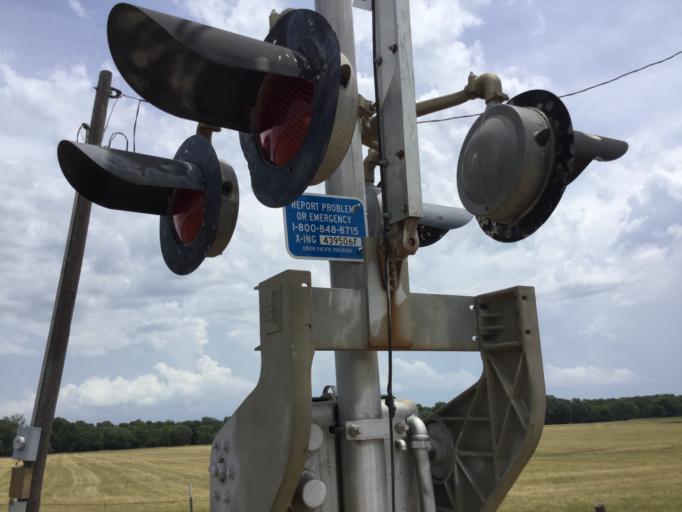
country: US
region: Kansas
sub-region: Woodson County
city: Yates Center
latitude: 37.9729
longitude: -95.6654
